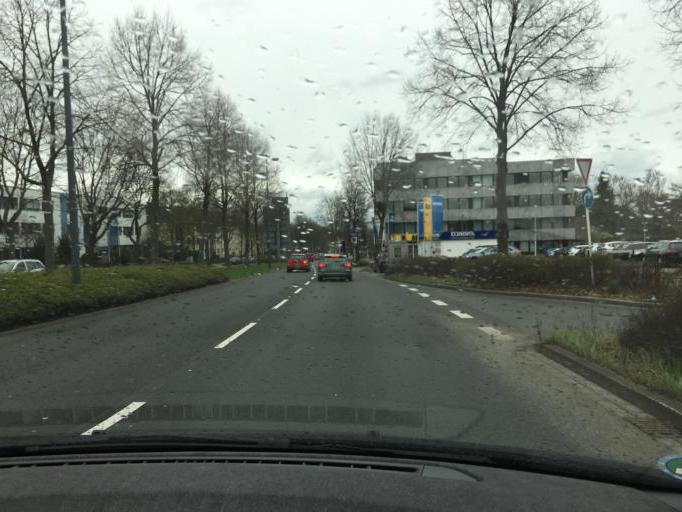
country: DE
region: North Rhine-Westphalia
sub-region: Regierungsbezirk Arnsberg
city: Dortmund
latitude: 51.4995
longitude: 7.4683
